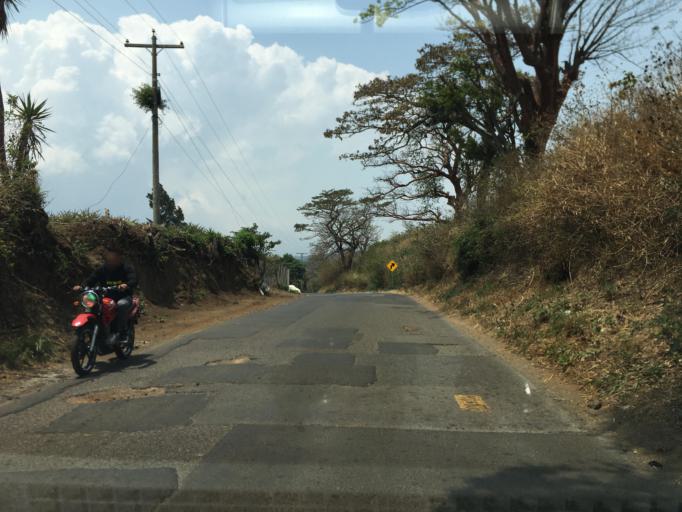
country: GT
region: Escuintla
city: San Vicente Pacaya
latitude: 14.3776
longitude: -90.5538
